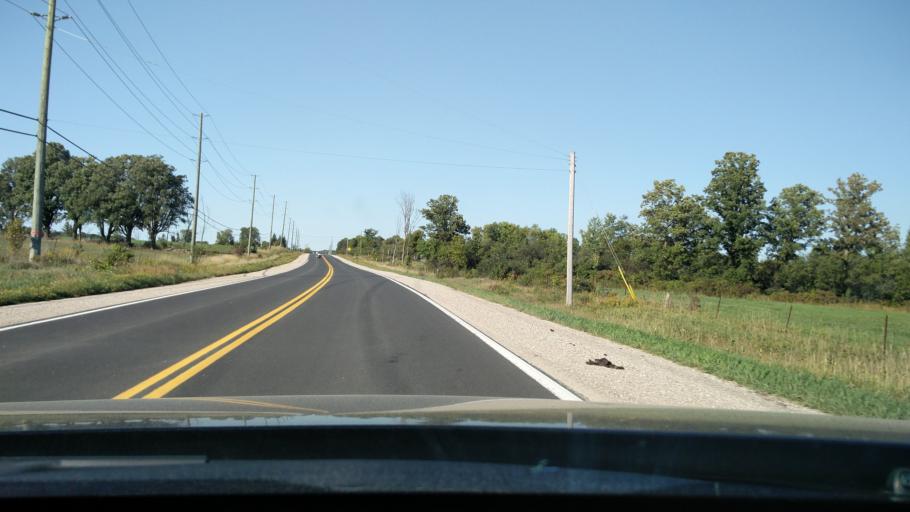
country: CA
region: Ontario
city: Perth
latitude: 44.8392
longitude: -76.3071
